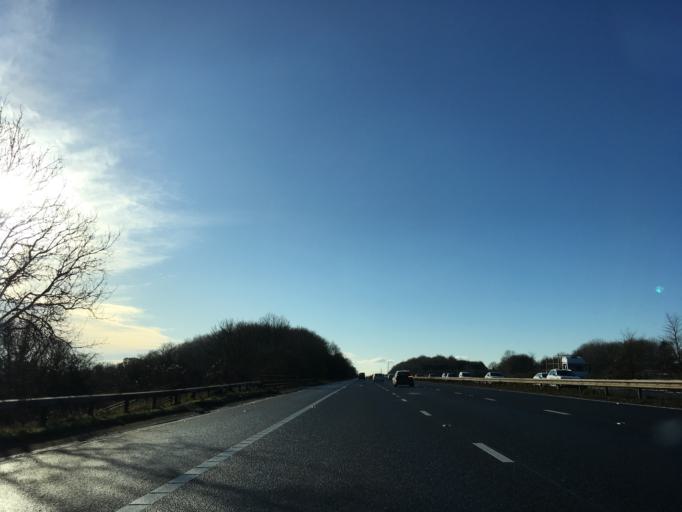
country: GB
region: England
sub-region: South Gloucestershire
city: Tytherington
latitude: 51.5997
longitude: -2.4817
